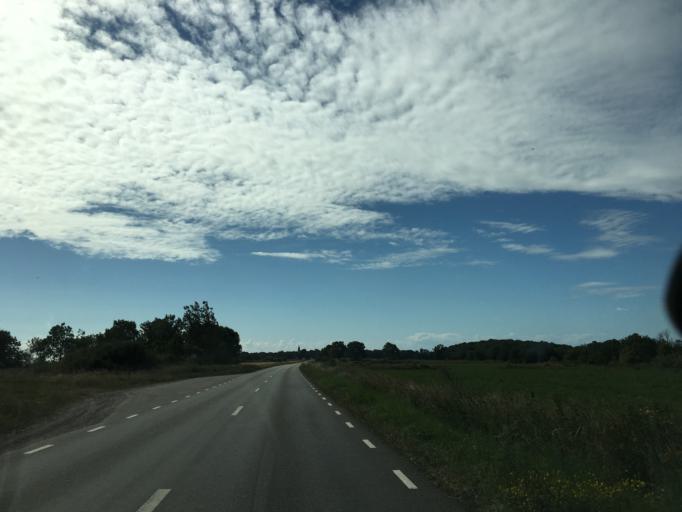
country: SE
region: Kalmar
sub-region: Morbylanga Kommun
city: Moerbylanga
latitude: 56.4736
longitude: 16.4295
